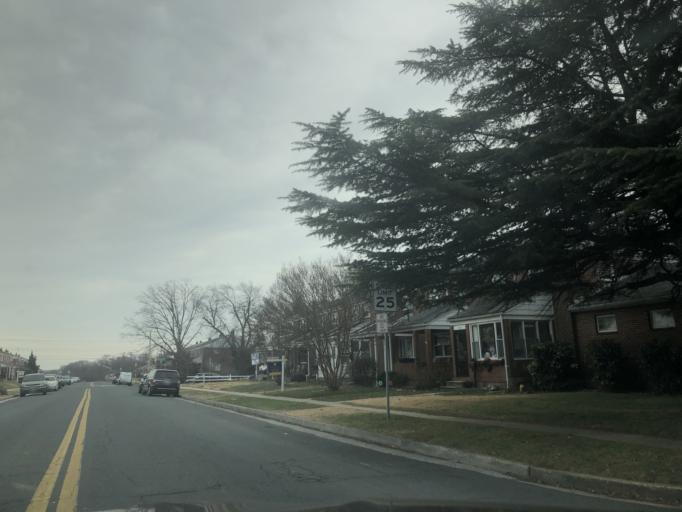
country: US
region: Maryland
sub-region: Baltimore County
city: Dundalk
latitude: 39.2631
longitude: -76.5049
